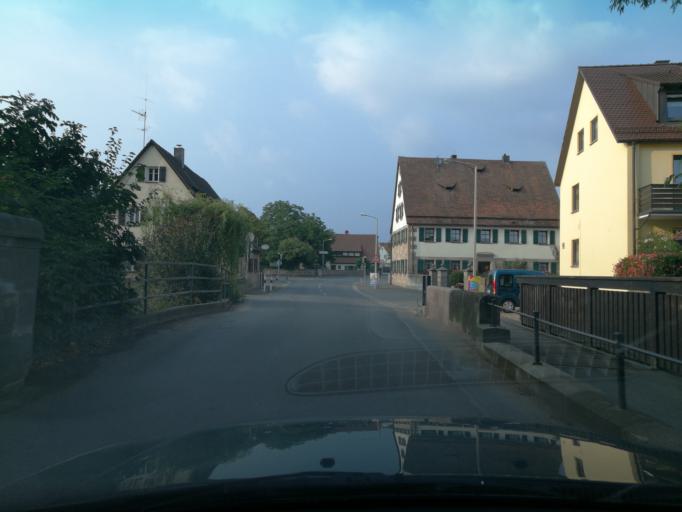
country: DE
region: Bavaria
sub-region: Regierungsbezirk Mittelfranken
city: Wetzendorf
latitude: 49.5130
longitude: 11.0461
